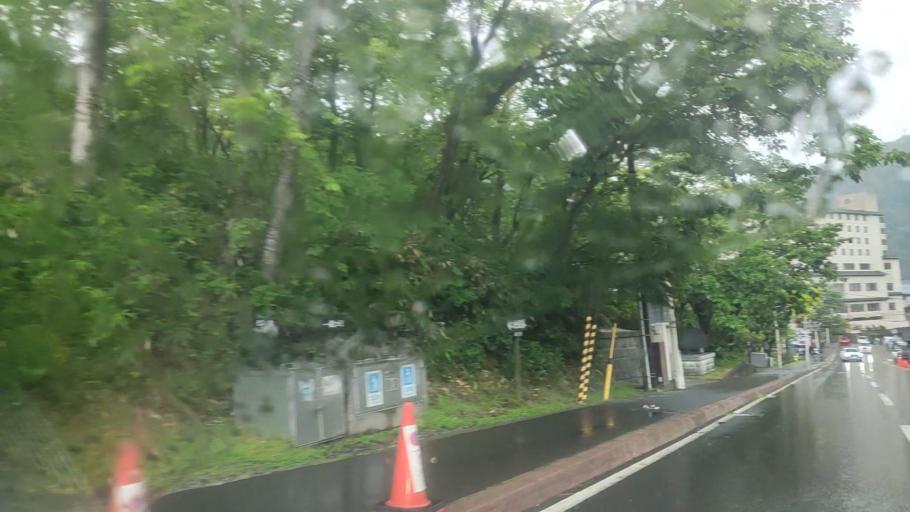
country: JP
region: Hokkaido
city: Shiraoi
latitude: 42.4970
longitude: 141.1458
